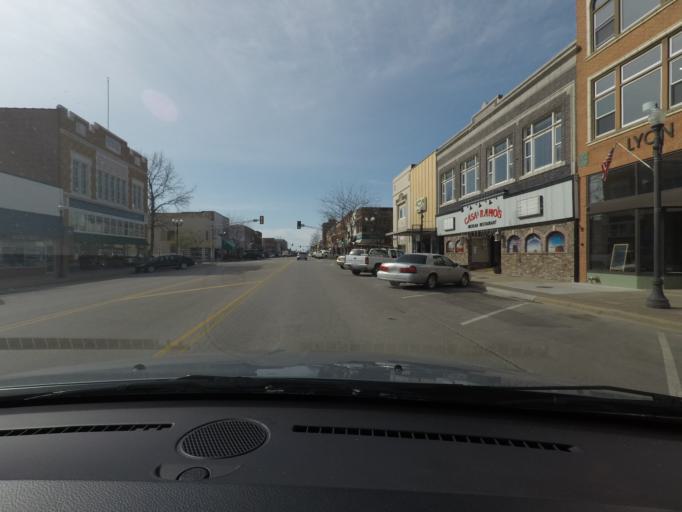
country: US
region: Kansas
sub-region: Lyon County
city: Emporia
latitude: 38.4067
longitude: -96.1802
